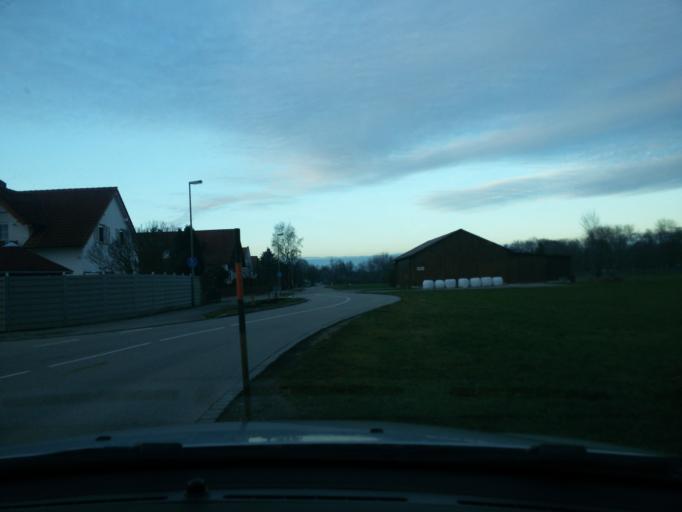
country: DE
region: Bavaria
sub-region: Swabia
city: Schwabmunchen
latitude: 48.1690
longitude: 10.7506
